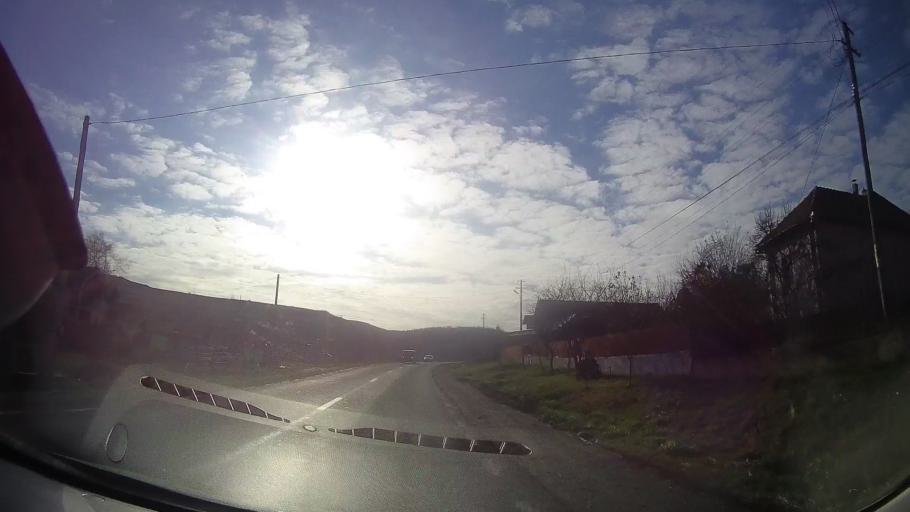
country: RO
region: Cluj
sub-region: Comuna Cojocna
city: Cojocna
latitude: 46.8080
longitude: 23.8489
